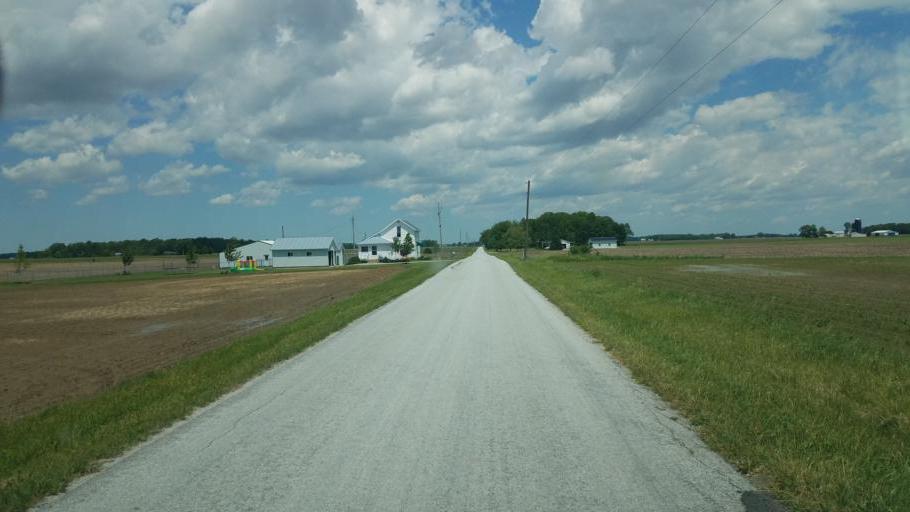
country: US
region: Ohio
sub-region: Hardin County
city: Kenton
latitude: 40.6642
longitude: -83.4773
